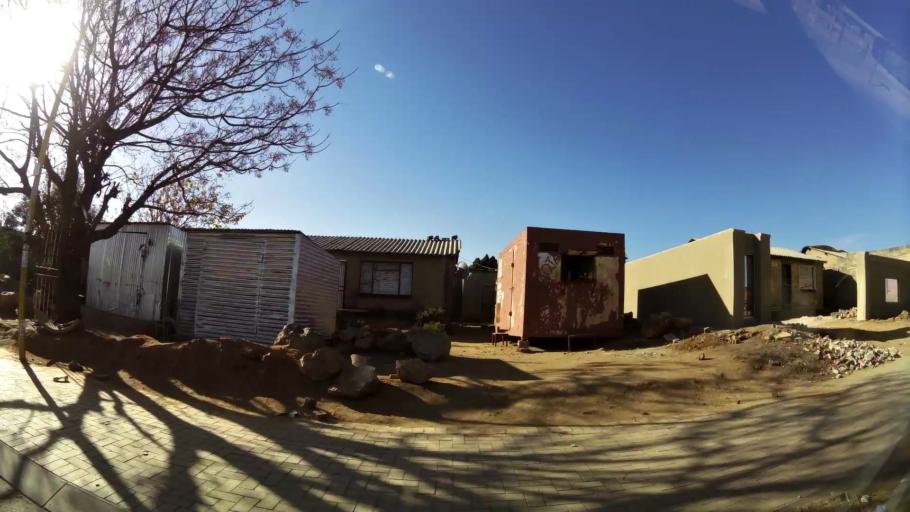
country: ZA
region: Gauteng
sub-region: Ekurhuleni Metropolitan Municipality
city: Tembisa
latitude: -26.0279
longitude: 28.2134
